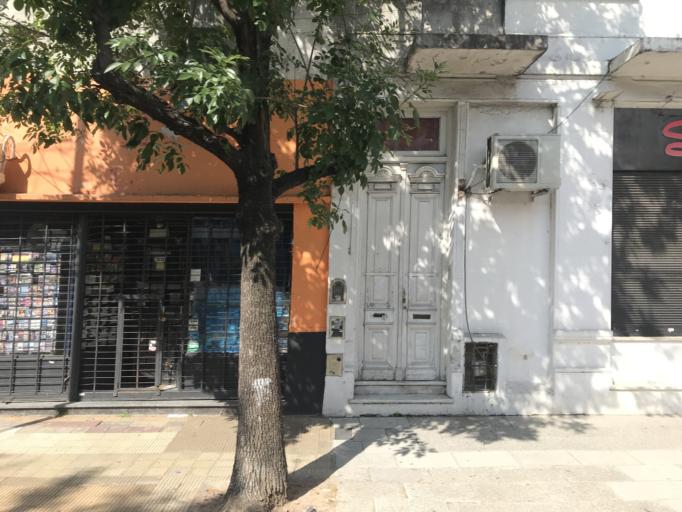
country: AR
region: Buenos Aires F.D.
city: Villa Santa Rita
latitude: -34.6333
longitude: -58.4365
